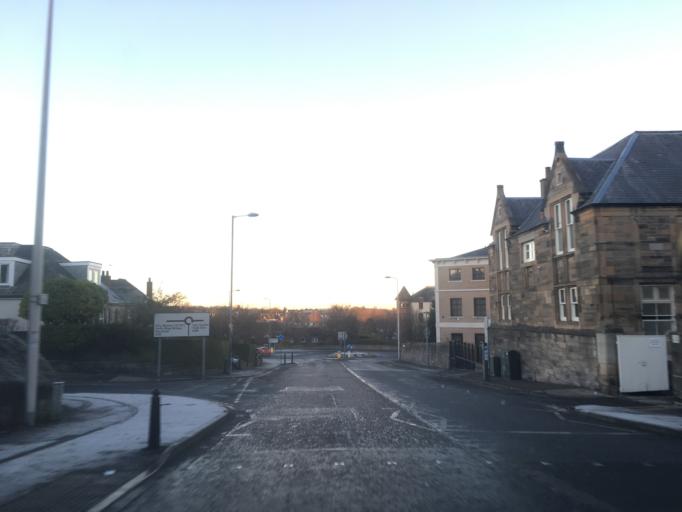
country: GB
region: Scotland
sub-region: Edinburgh
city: Edinburgh
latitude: 55.9539
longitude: -3.2297
